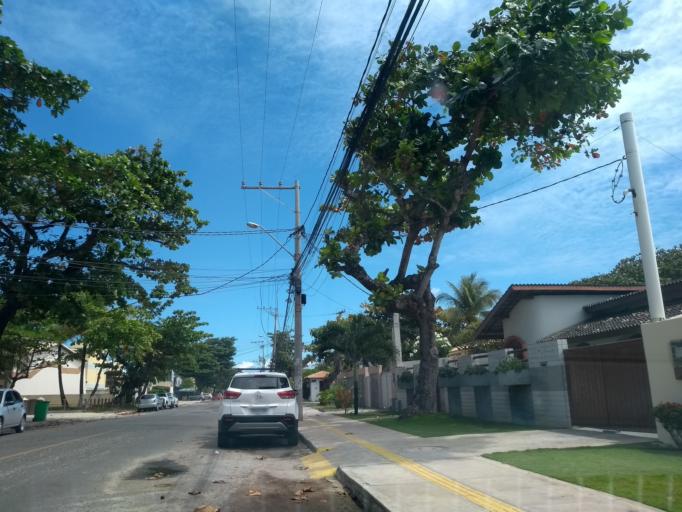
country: BR
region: Bahia
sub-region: Lauro De Freitas
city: Lauro de Freitas
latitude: -12.9312
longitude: -38.3230
